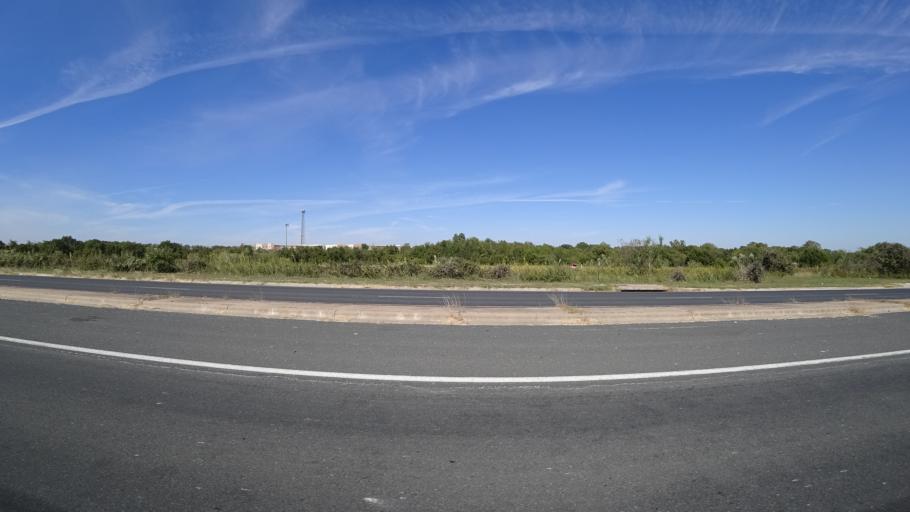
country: US
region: Texas
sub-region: Travis County
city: Austin
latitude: 30.1897
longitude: -97.7034
